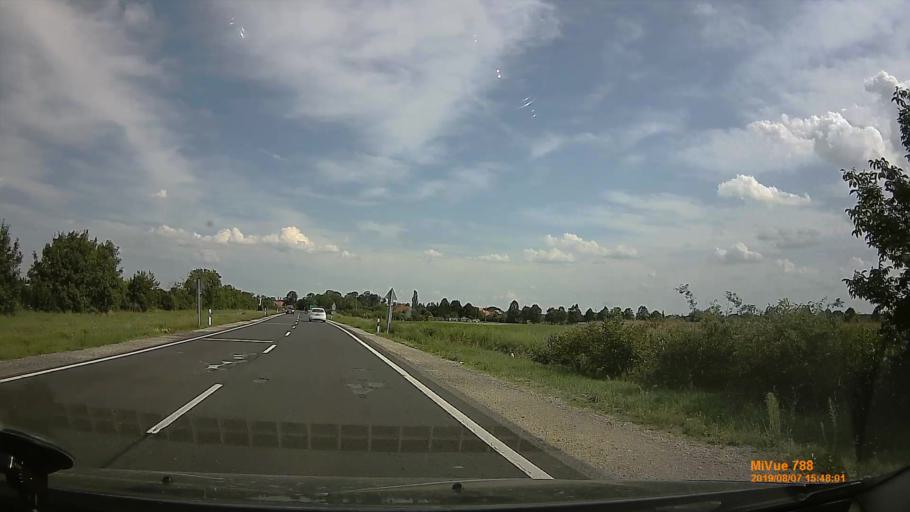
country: HU
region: Vas
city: Jak
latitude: 47.1648
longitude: 16.6328
